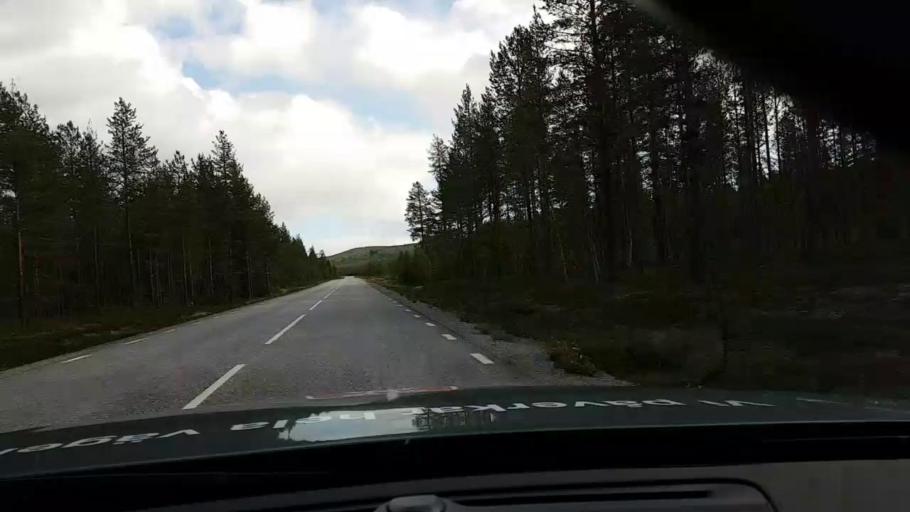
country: SE
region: Vaesternorrland
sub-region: OErnskoeldsviks Kommun
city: Bredbyn
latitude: 63.6844
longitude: 17.7774
